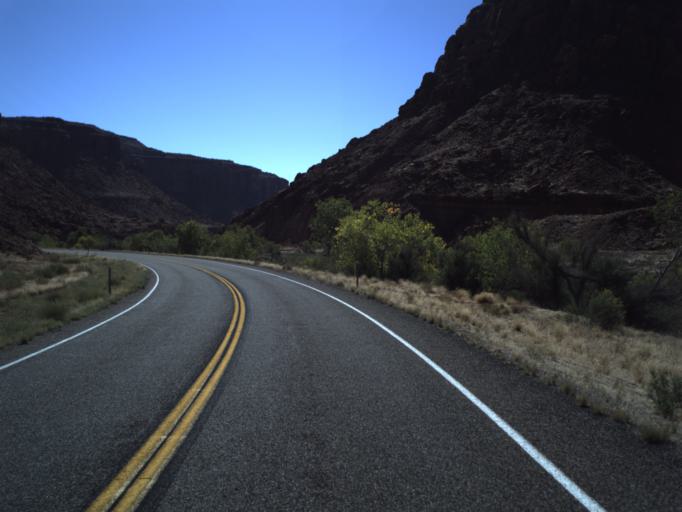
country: US
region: Utah
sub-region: San Juan County
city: Blanding
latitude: 37.9474
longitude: -110.4757
